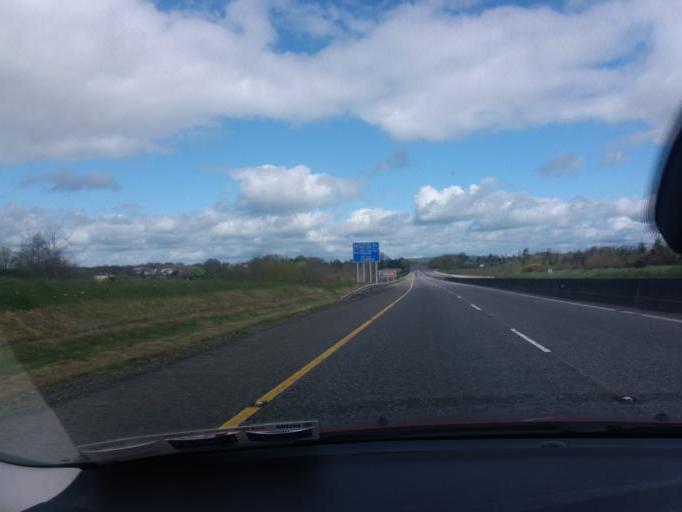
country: IE
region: Munster
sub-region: County Cork
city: Fermoy
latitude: 52.1366
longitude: -8.2608
